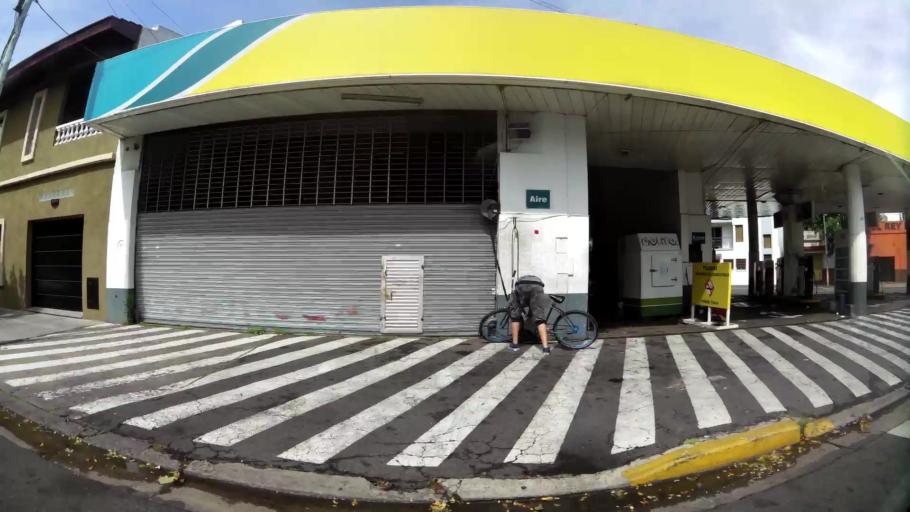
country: AR
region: Buenos Aires
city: San Justo
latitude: -34.6497
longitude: -58.5241
